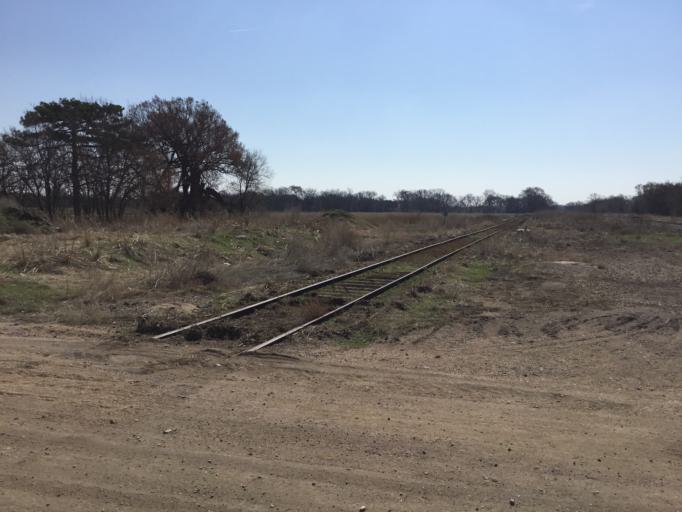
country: US
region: Kansas
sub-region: Ellsworth County
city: Ellsworth
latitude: 38.7581
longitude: -98.3625
